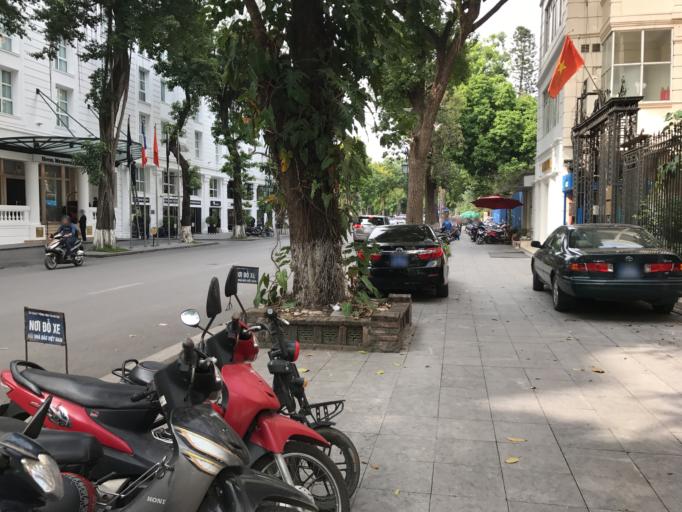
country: VN
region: Ha Noi
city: Hoan Kiem
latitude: 21.0253
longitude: 105.8567
